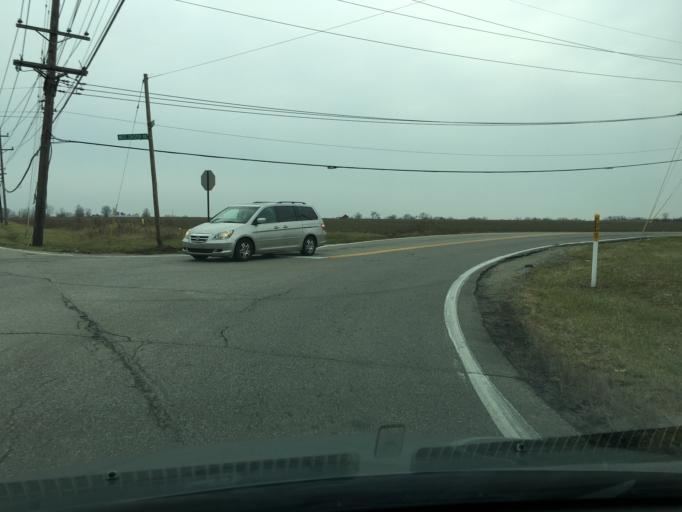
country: US
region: Ohio
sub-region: Hamilton County
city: Highpoint
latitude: 39.3179
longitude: -84.3510
